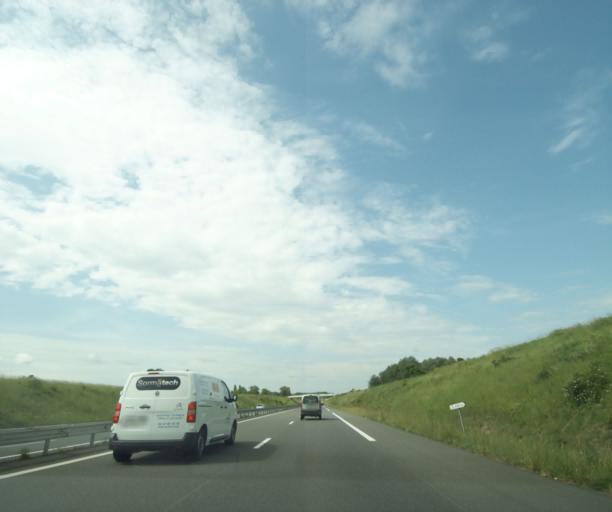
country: FR
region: Pays de la Loire
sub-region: Departement de Maine-et-Loire
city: Saint-Philbert-du-Peuple
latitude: 47.3680
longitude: -0.0836
